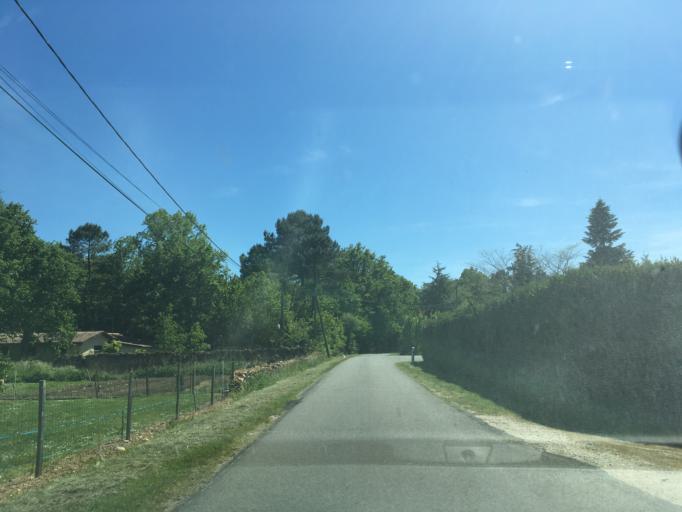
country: FR
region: Aquitaine
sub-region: Departement de la Gironde
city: Lesparre-Medoc
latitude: 45.2935
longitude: -0.8932
